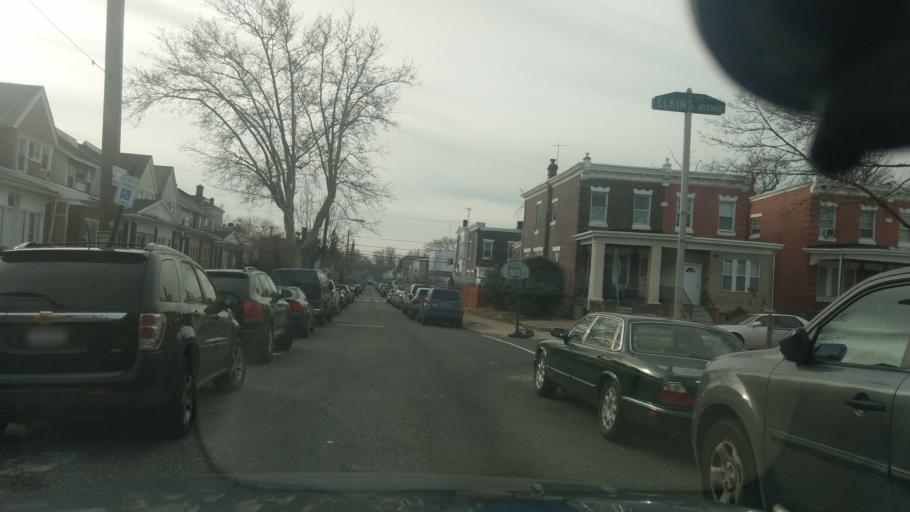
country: US
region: Pennsylvania
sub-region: Montgomery County
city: Jenkintown
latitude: 40.0375
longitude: -75.1313
